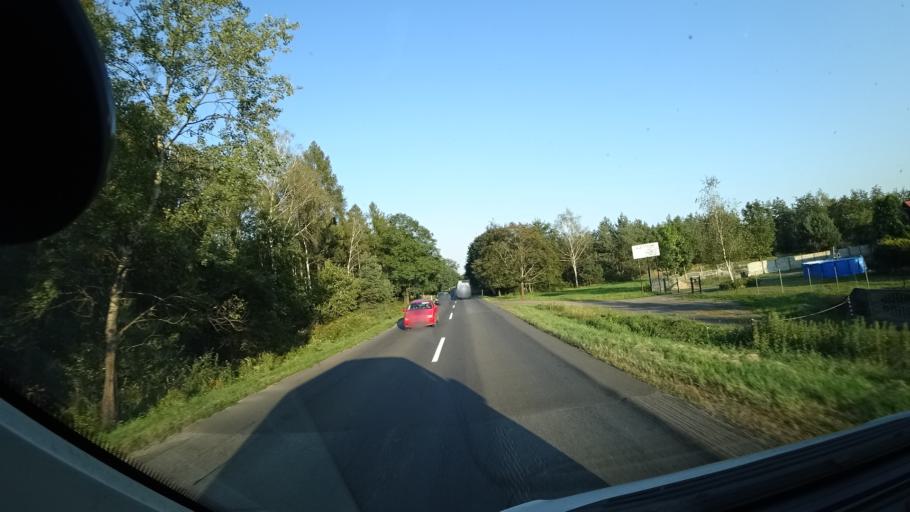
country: PL
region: Opole Voivodeship
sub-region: Powiat kedzierzynsko-kozielski
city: Dziergowice
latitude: 50.2817
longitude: 18.3256
